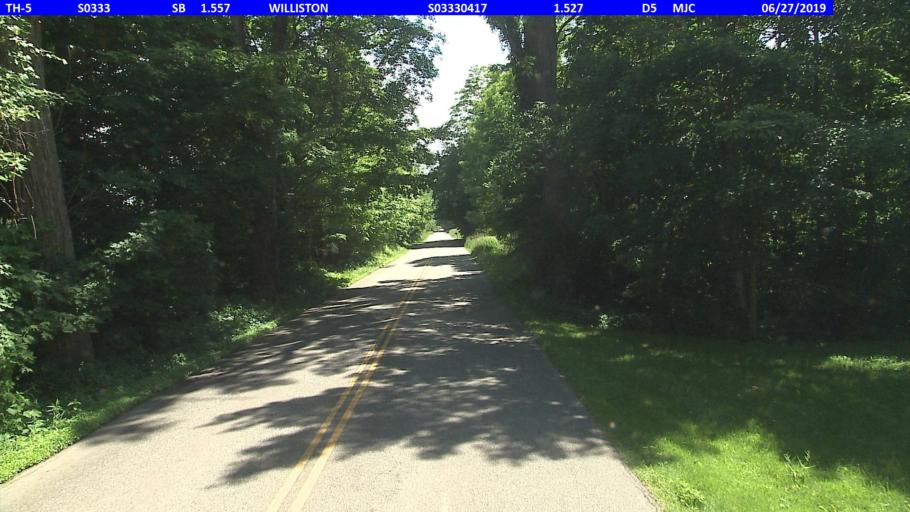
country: US
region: Vermont
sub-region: Chittenden County
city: South Burlington
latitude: 44.4231
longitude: -73.1352
